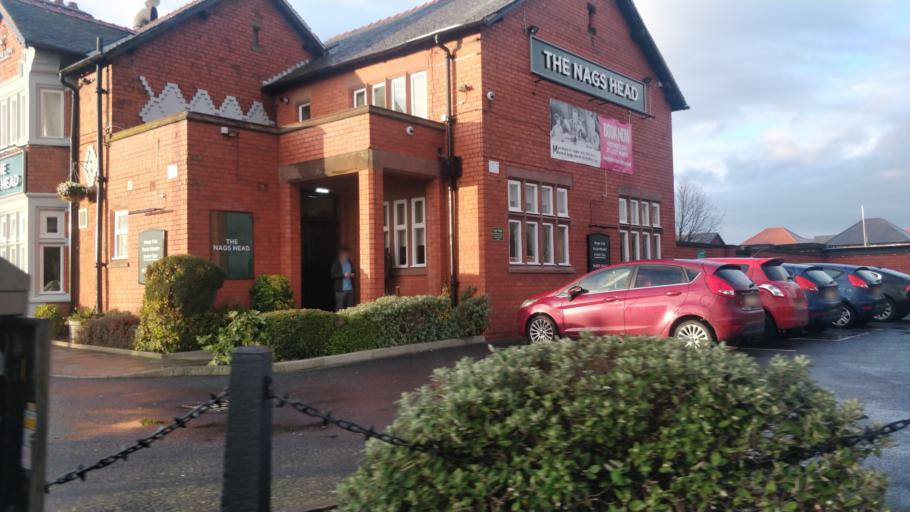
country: GB
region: England
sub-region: Sefton
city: Thornton
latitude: 53.5012
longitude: -3.0004
